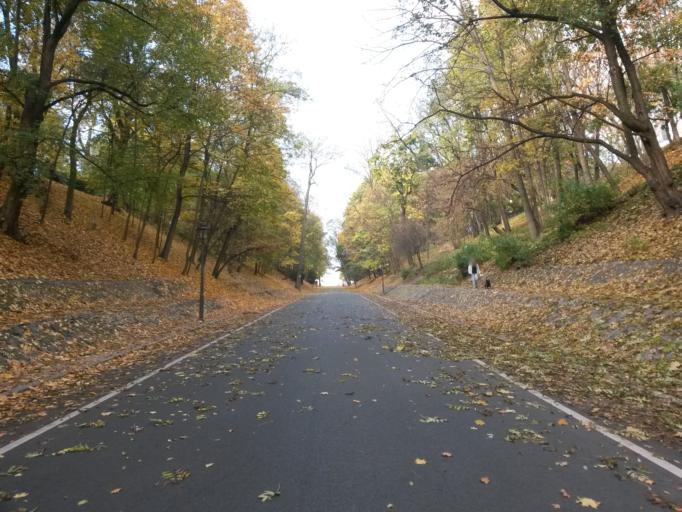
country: PL
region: Masovian Voivodeship
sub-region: Warszawa
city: Srodmiescie
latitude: 52.2181
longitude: 21.0303
